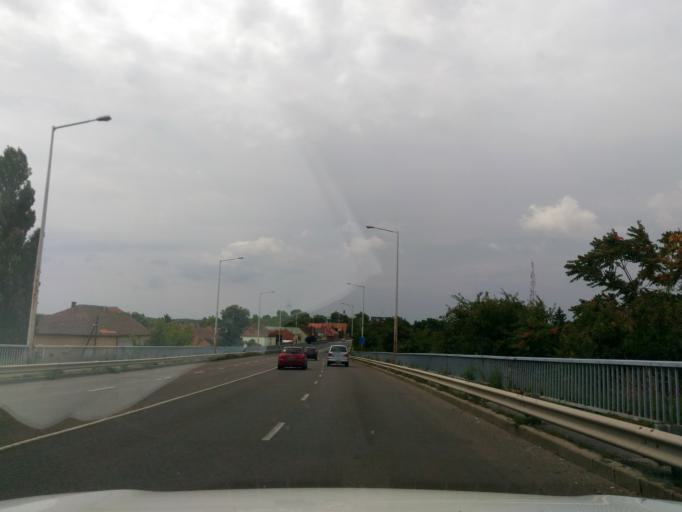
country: HU
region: Jasz-Nagykun-Szolnok
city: Szolnok
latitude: 47.1758
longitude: 20.1690
